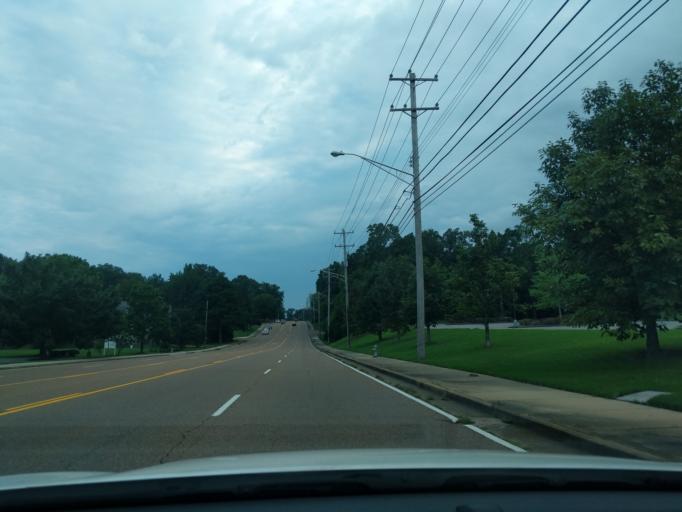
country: US
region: Tennessee
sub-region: Shelby County
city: Germantown
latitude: 35.0836
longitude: -89.8115
